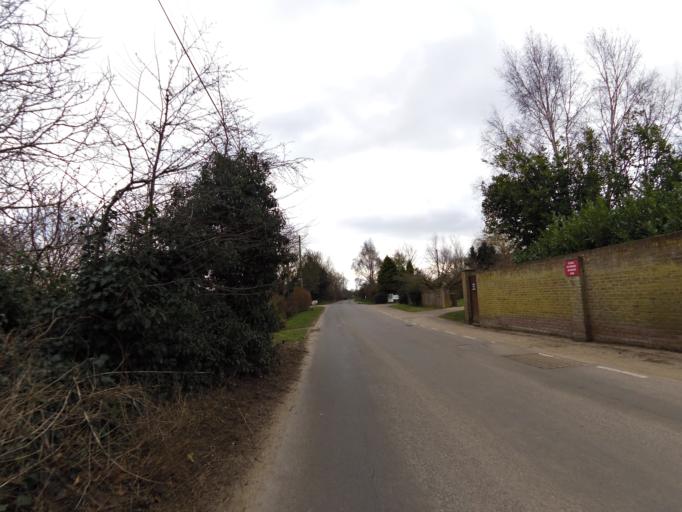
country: GB
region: England
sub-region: Suffolk
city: Woodbridge
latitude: 52.0379
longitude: 1.3142
